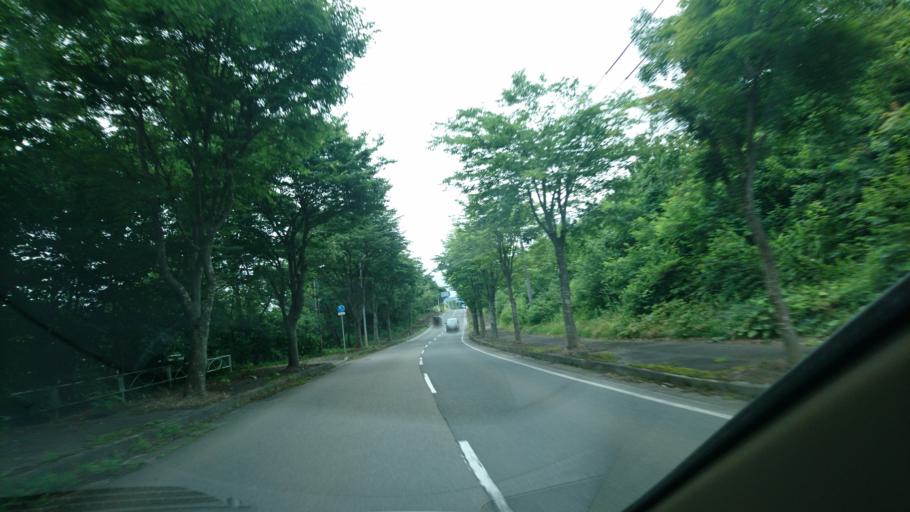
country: JP
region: Iwate
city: Mizusawa
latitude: 39.2096
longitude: 141.1761
